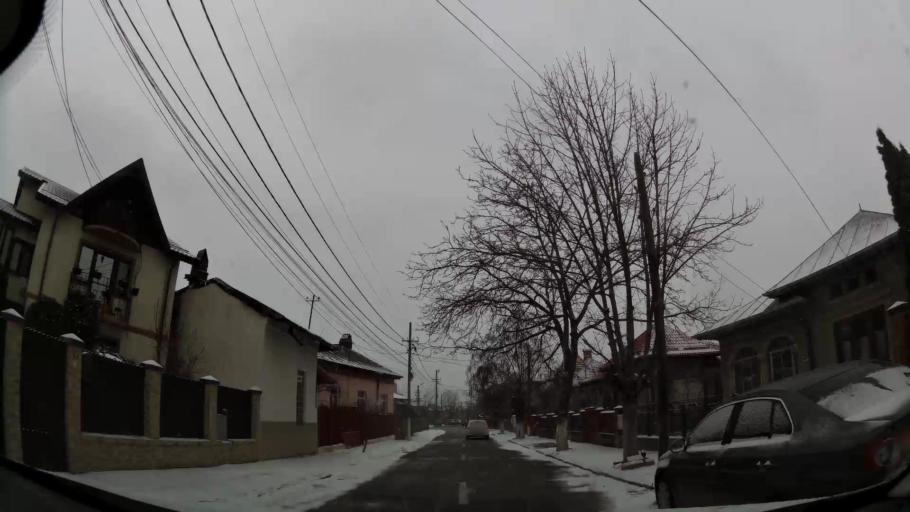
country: RO
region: Dambovita
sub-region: Municipiul Targoviste
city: Targoviste
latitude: 44.9363
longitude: 25.4538
